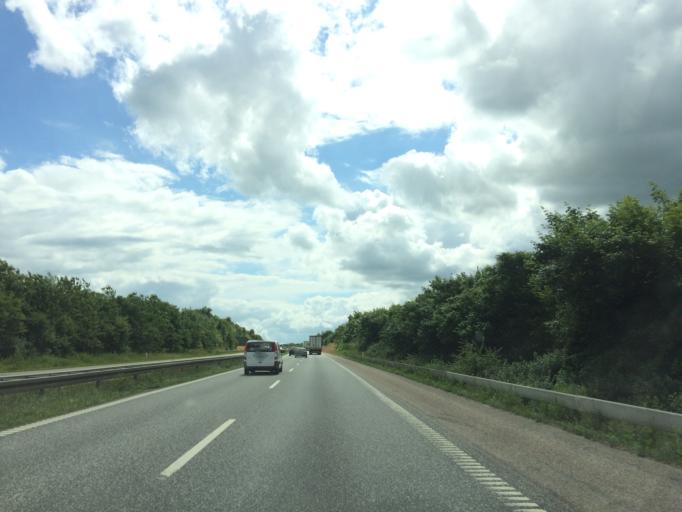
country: DK
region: North Denmark
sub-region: Mariagerfjord Kommune
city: Hobro
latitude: 56.7747
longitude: 9.6943
